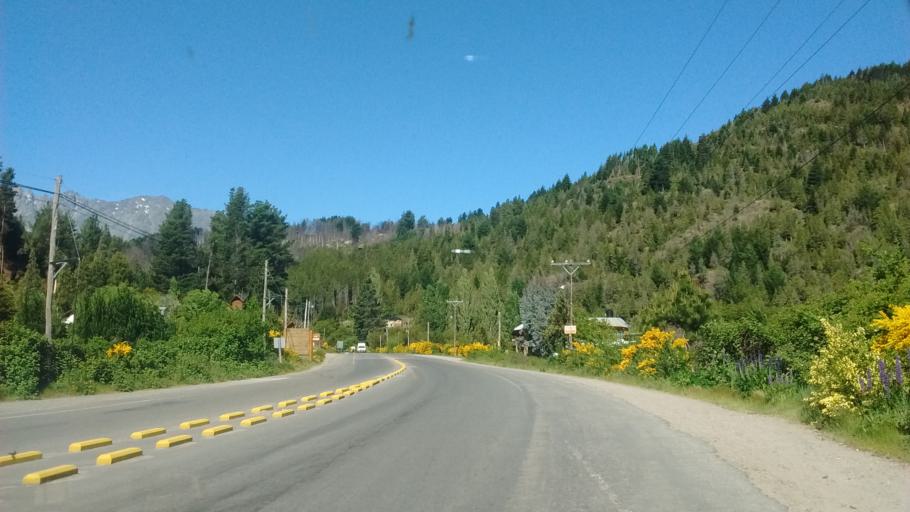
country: AR
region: Chubut
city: Lago Puelo
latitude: -42.0334
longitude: -71.5855
